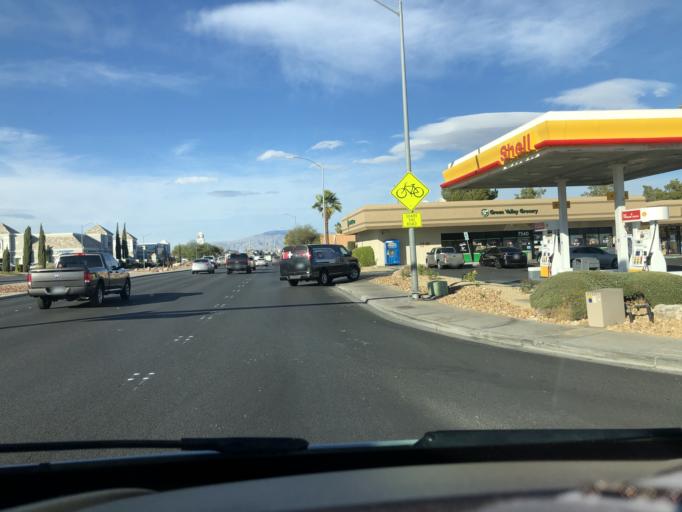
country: US
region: Nevada
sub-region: Clark County
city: Spring Valley
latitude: 36.1740
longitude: -115.2596
